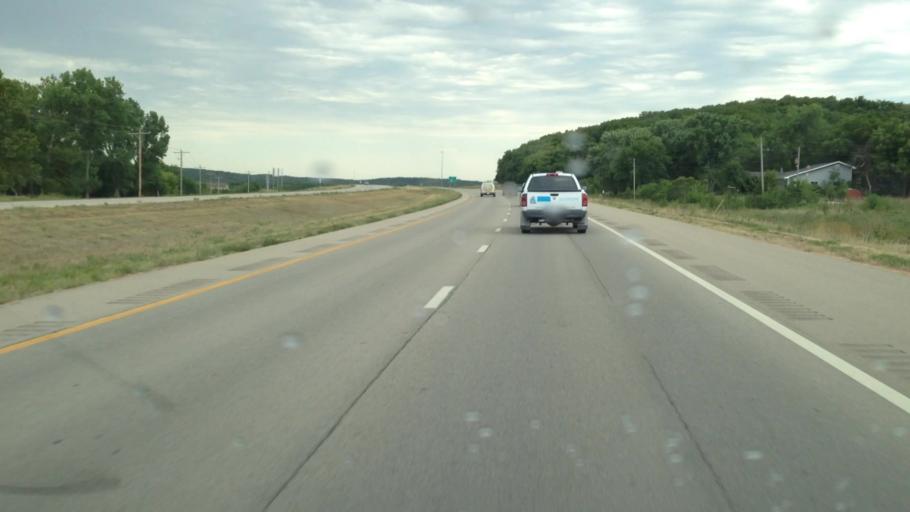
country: US
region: Kansas
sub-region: Douglas County
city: Lawrence
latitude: 38.8935
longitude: -95.2607
